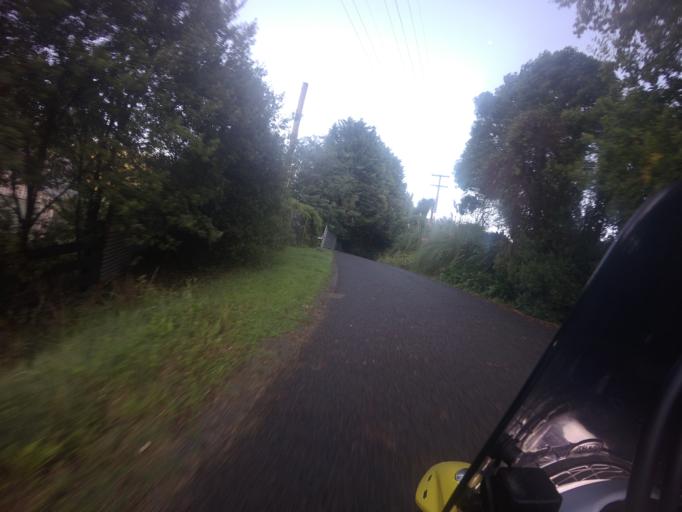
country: NZ
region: Gisborne
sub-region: Gisborne District
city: Gisborne
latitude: -38.6593
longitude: 178.0544
